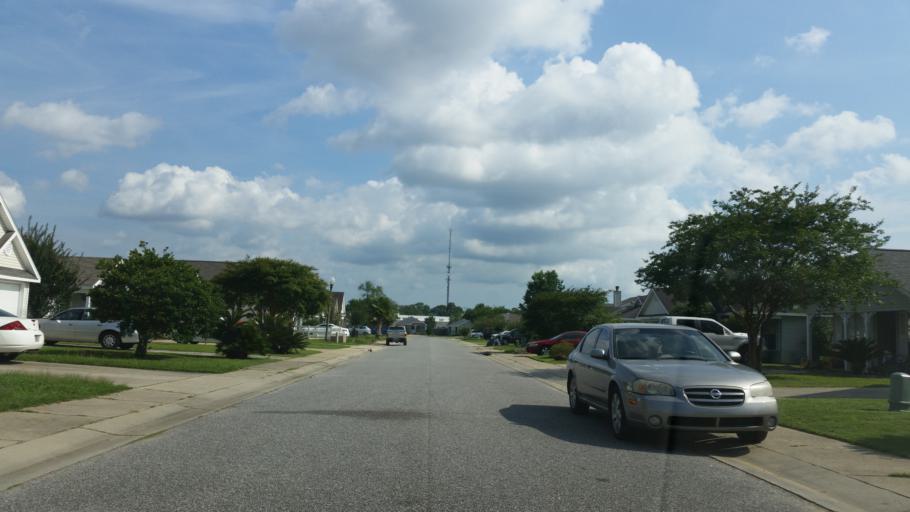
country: US
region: Florida
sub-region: Escambia County
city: Ensley
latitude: 30.5389
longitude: -87.3114
